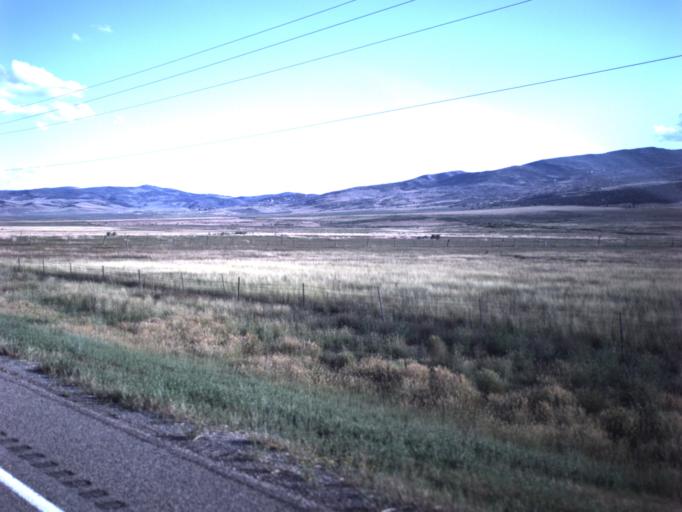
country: US
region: Utah
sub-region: Sanpete County
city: Fairview
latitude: 39.8025
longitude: -111.5022
